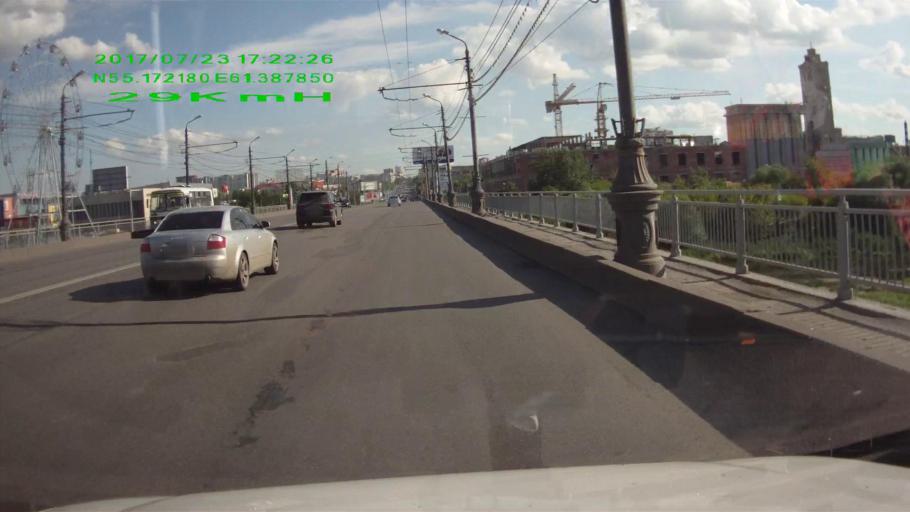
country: RU
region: Chelyabinsk
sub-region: Gorod Chelyabinsk
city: Chelyabinsk
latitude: 55.1719
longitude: 61.3878
